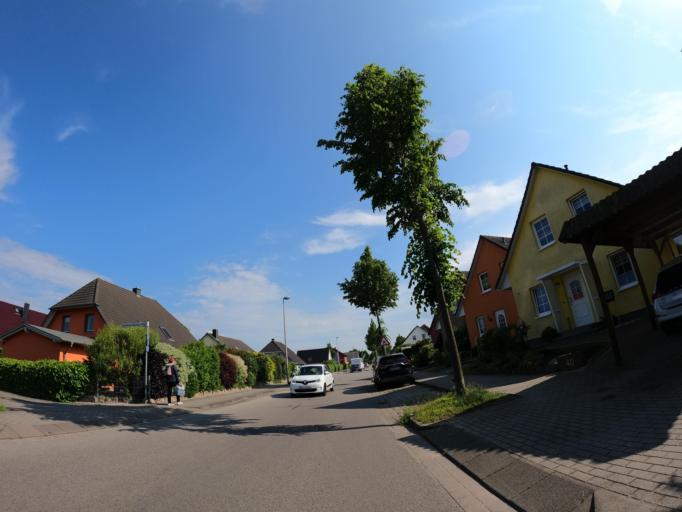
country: DE
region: Mecklenburg-Vorpommern
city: Stralsund
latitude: 54.2947
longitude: 13.0669
